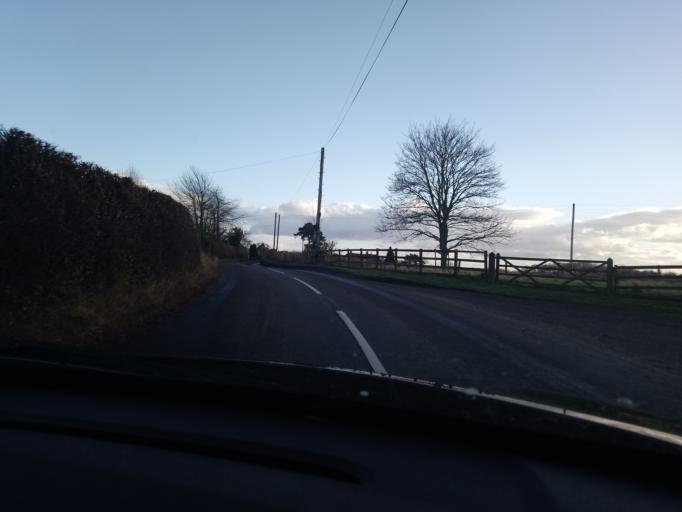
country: GB
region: England
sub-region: Shropshire
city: Petton
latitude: 52.8904
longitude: -2.7927
